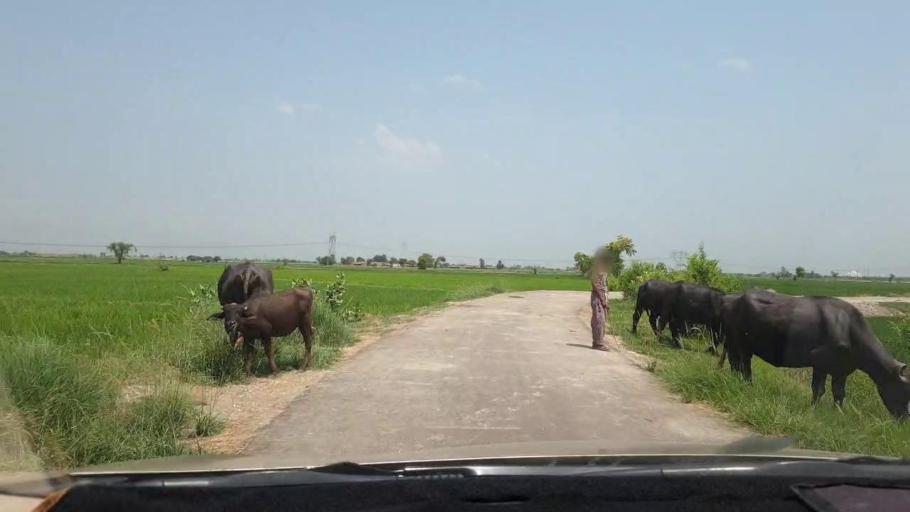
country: PK
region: Sindh
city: Naudero
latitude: 27.6675
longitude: 68.3239
